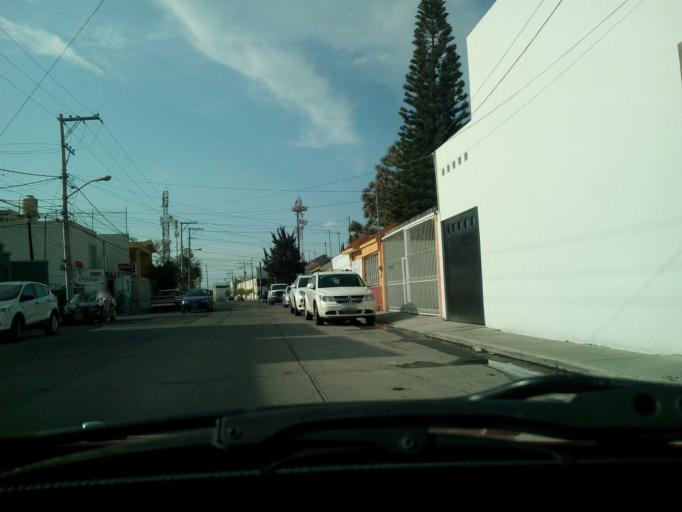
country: MX
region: Aguascalientes
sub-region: Aguascalientes
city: Aguascalientes
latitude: 21.9066
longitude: -102.2948
